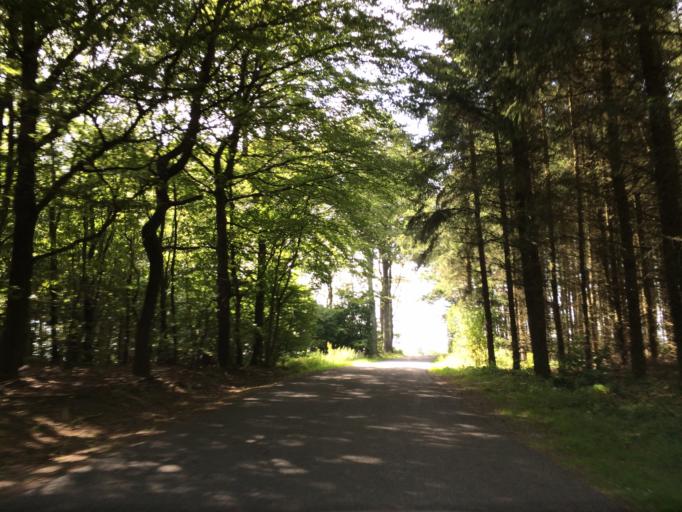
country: DK
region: Central Jutland
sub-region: Skanderborg Kommune
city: Galten
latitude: 56.1627
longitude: 9.8517
